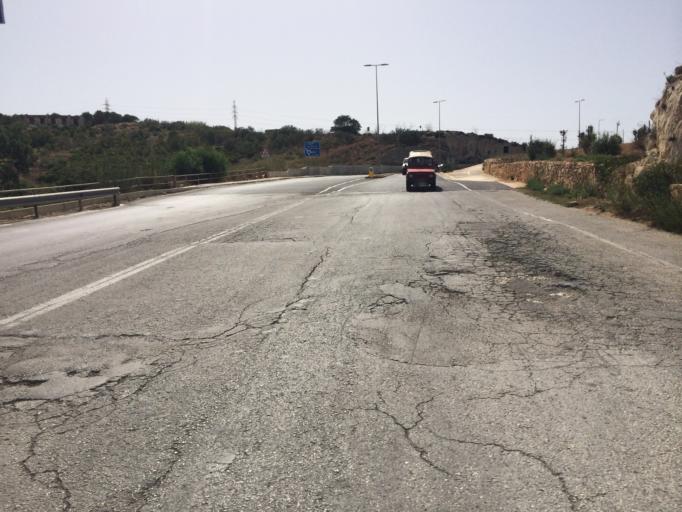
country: MT
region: Il-Mellieha
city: Mellieha
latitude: 35.9758
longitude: 14.3475
